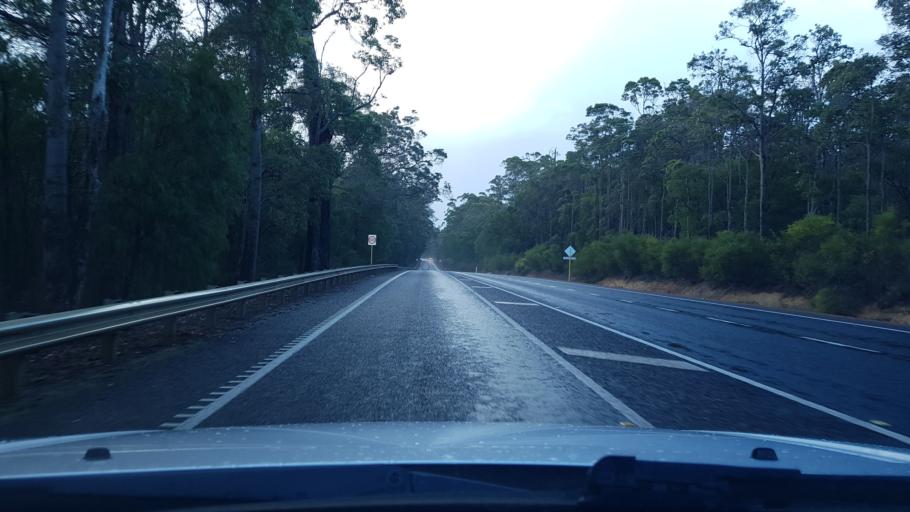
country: AU
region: Western Australia
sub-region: Augusta-Margaret River Shire
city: Margaret River
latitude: -33.9150
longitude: 115.0828
